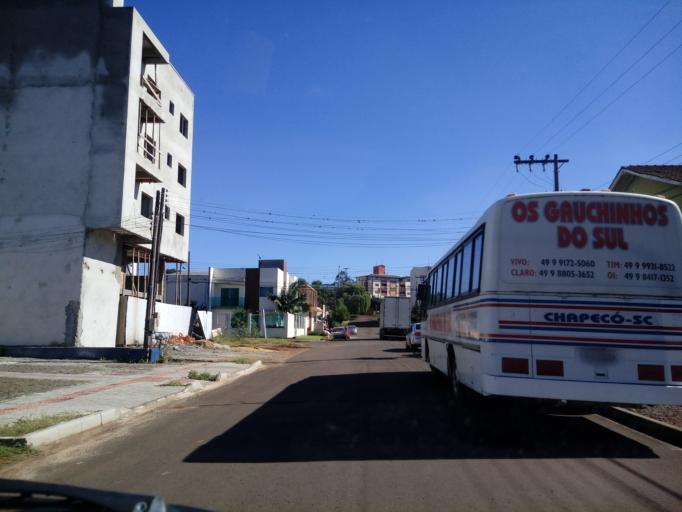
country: BR
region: Santa Catarina
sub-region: Chapeco
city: Chapeco
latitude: -27.0957
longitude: -52.6358
